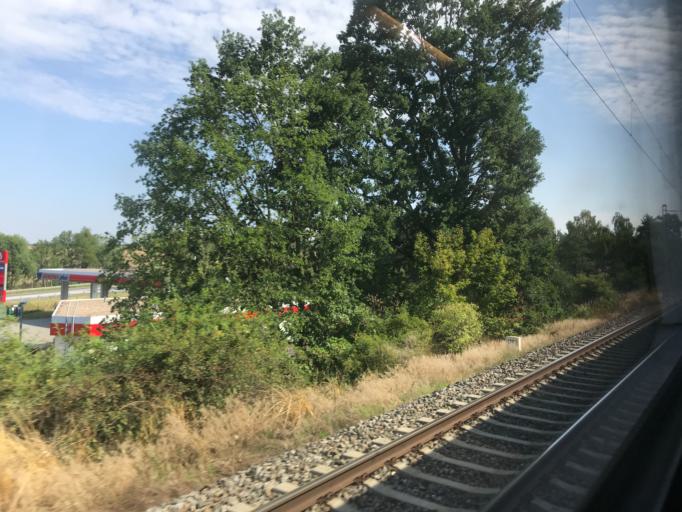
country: CZ
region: Central Bohemia
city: Bystrice
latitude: 49.7440
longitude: 14.6719
